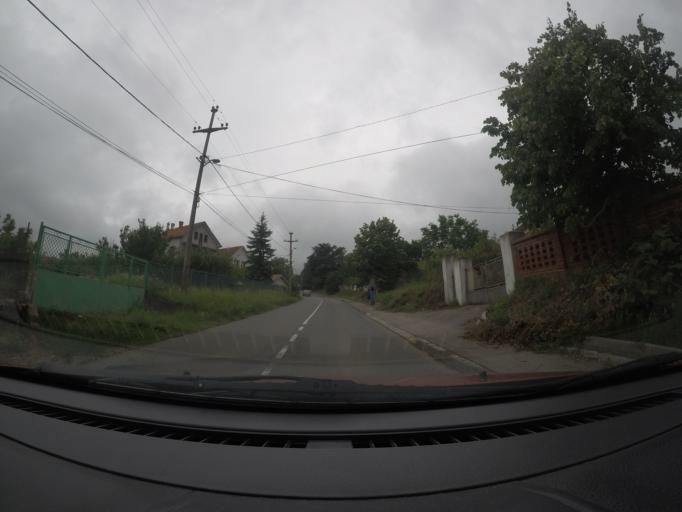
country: RS
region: Central Serbia
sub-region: Belgrade
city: Zvezdara
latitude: 44.6972
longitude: 20.5549
